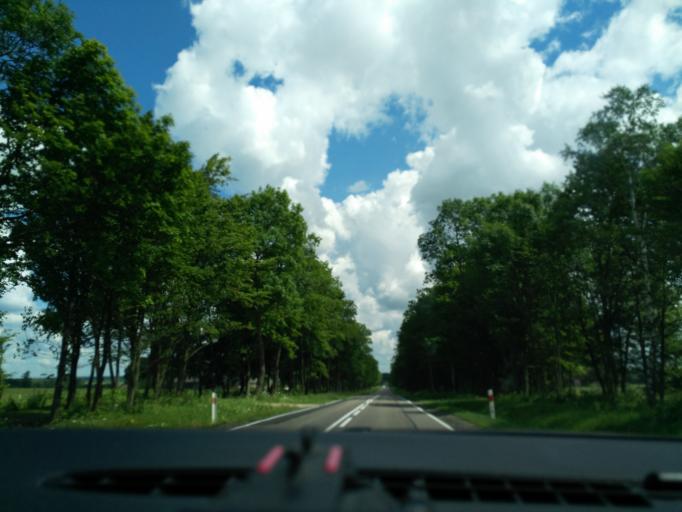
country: PL
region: Podlasie
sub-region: Powiat bielski
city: Bocki
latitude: 52.6161
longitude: 22.9947
